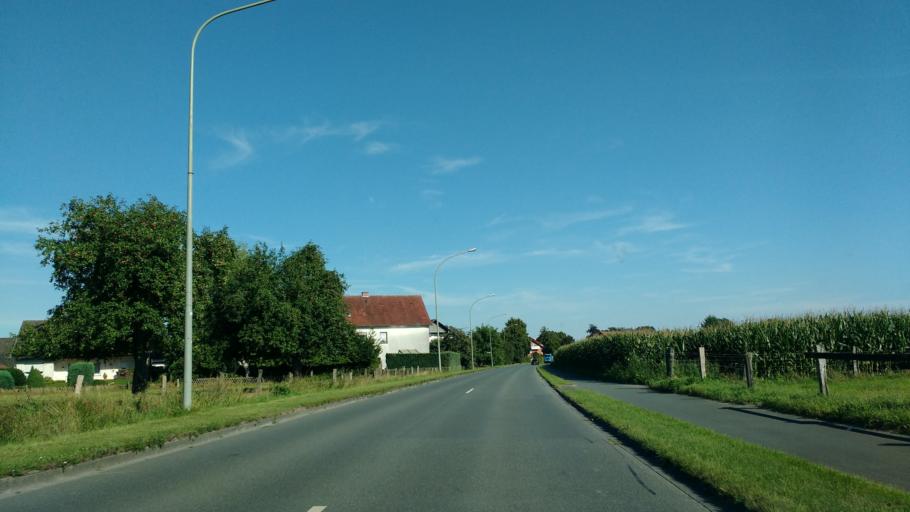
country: DE
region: North Rhine-Westphalia
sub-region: Regierungsbezirk Detmold
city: Hovelhof
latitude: 51.7392
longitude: 8.6678
